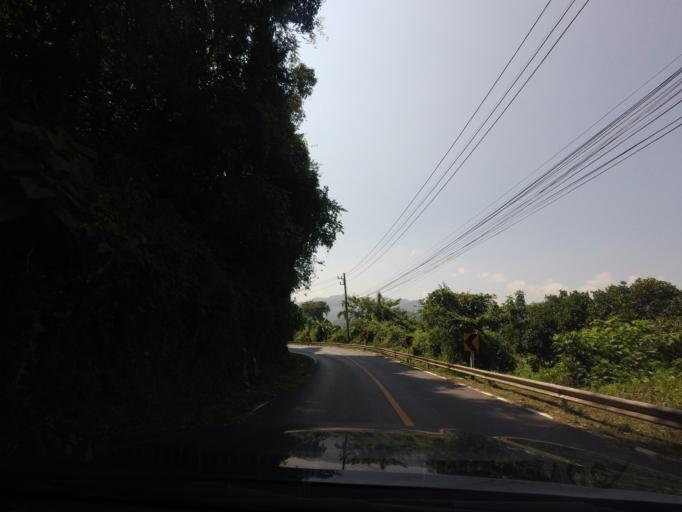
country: TH
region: Nan
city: Bo Kluea
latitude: 19.0874
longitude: 101.1533
